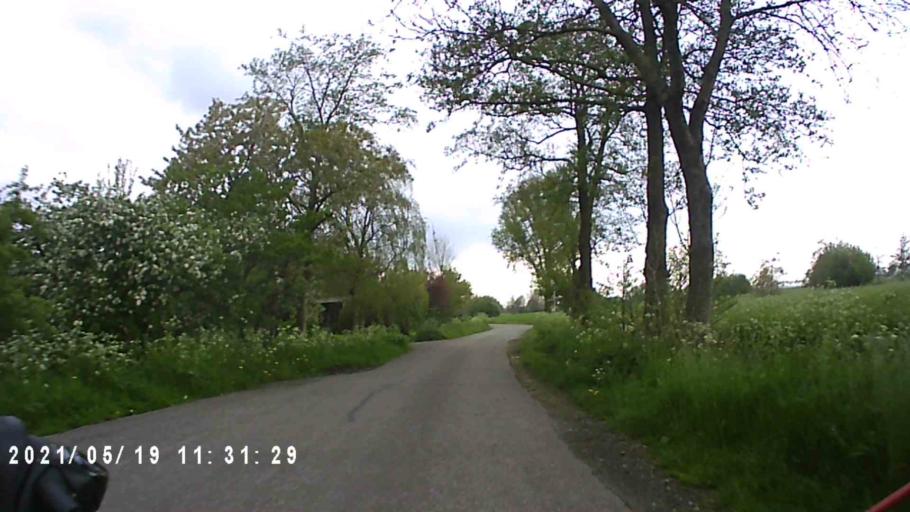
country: NL
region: Friesland
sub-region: Gemeente Kollumerland en Nieuwkruisland
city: Kollum
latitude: 53.2742
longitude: 6.1743
